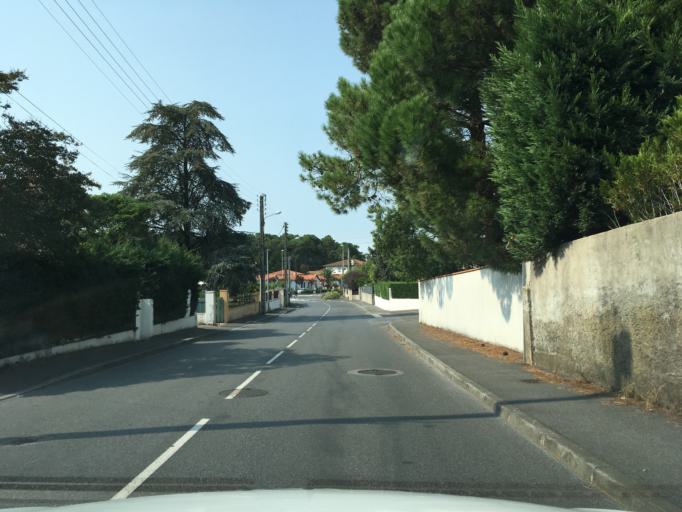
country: FR
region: Aquitaine
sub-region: Departement des Pyrenees-Atlantiques
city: Bayonne
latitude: 43.5100
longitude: -1.5031
